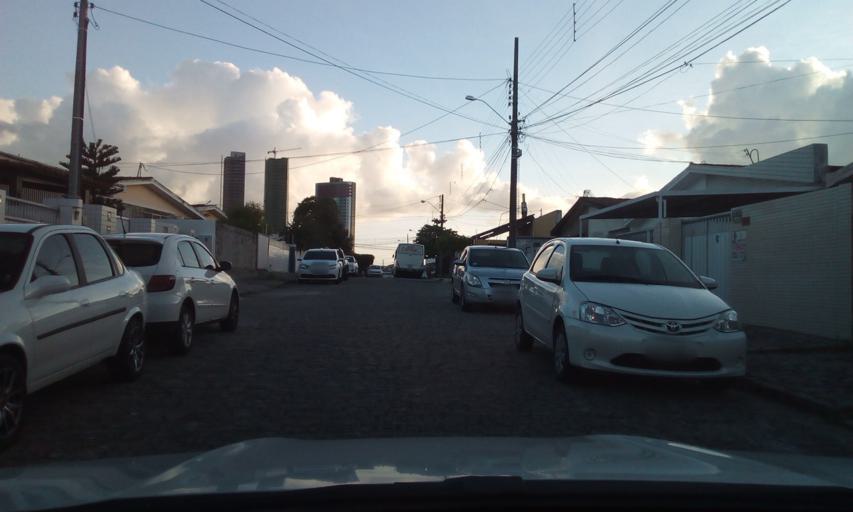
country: BR
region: Paraiba
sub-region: Joao Pessoa
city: Joao Pessoa
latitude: -7.1099
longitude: -34.8629
